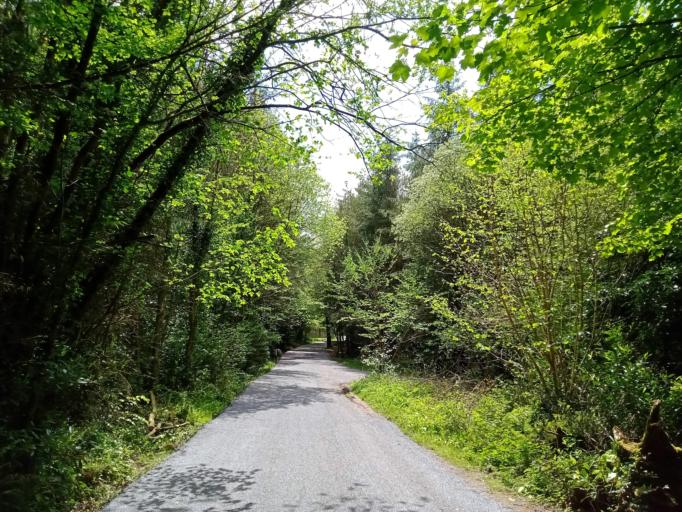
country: IE
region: Leinster
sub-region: Kilkenny
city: Castlecomer
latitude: 52.8104
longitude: -7.2028
